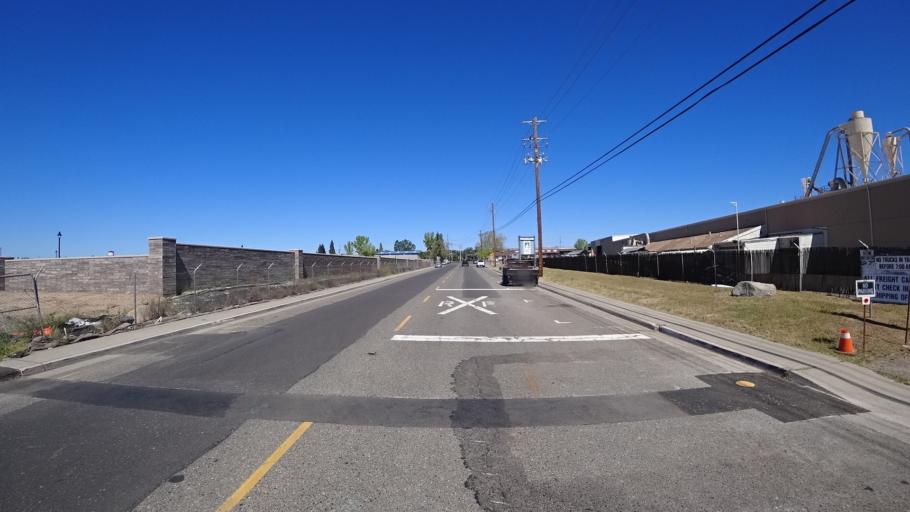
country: US
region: California
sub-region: Placer County
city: Rocklin
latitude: 38.8026
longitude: -121.2169
